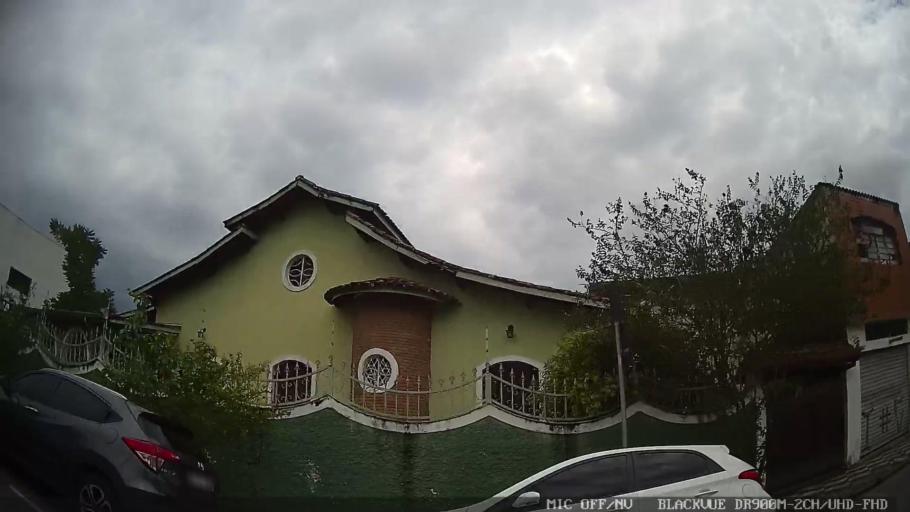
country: BR
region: Sao Paulo
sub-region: Caraguatatuba
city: Caraguatatuba
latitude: -23.6208
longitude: -45.4115
